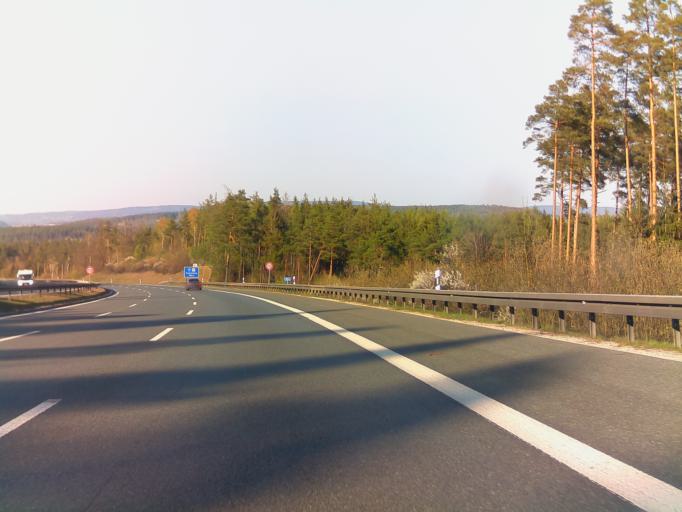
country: DE
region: Bavaria
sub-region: Upper Franconia
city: Haag
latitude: 49.8852
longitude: 11.5949
